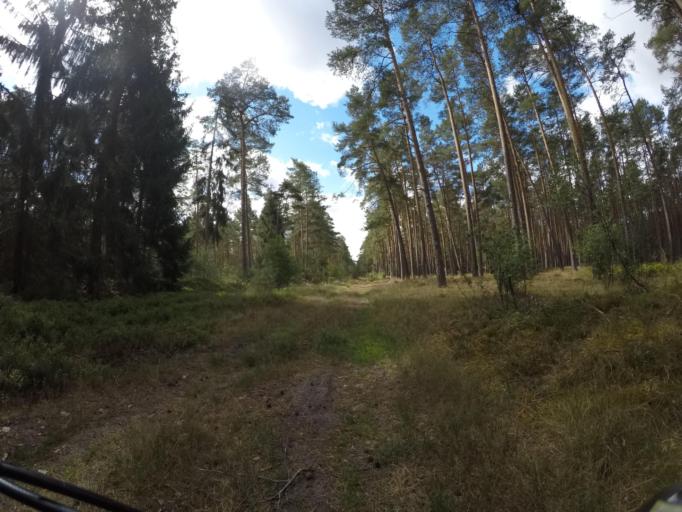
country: DE
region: Lower Saxony
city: Hitzacker
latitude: 53.2314
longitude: 11.0212
